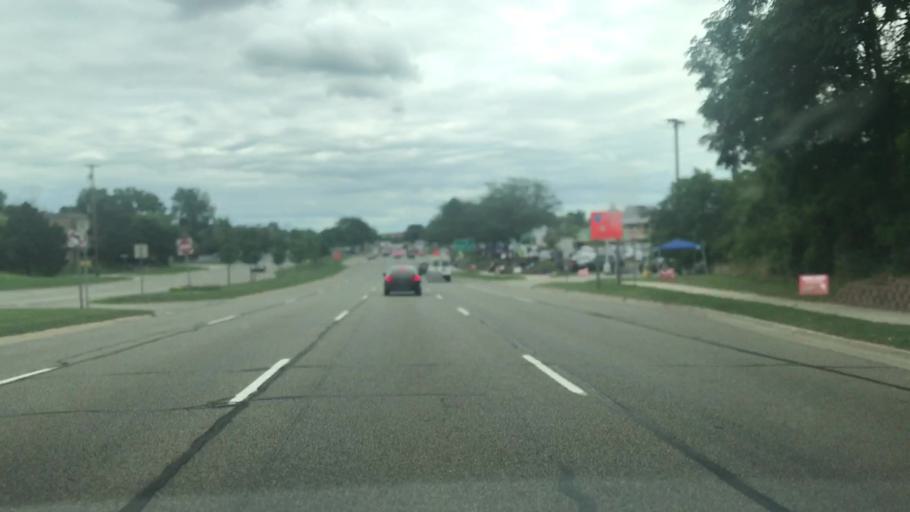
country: US
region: Michigan
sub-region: Oakland County
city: Bloomfield Hills
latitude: 42.6069
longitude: -83.2676
